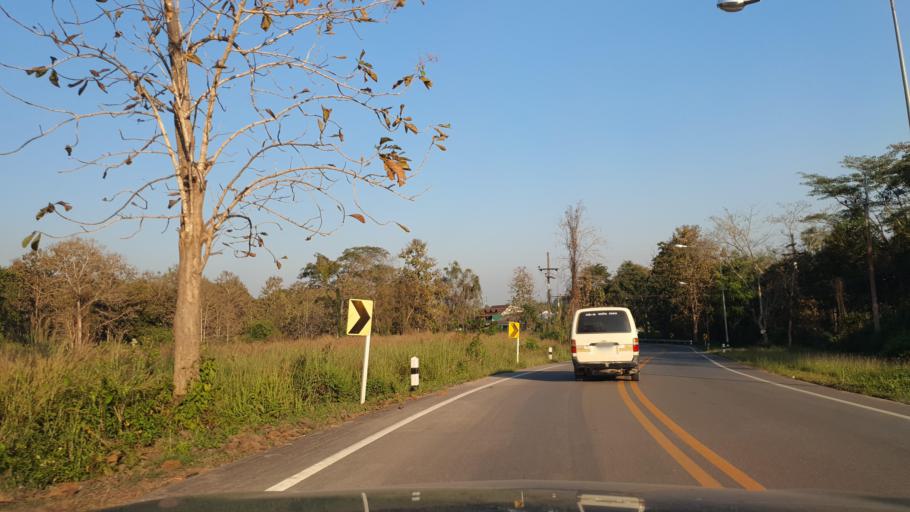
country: TH
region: Chiang Rai
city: Mae Lao
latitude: 19.8334
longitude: 99.6905
